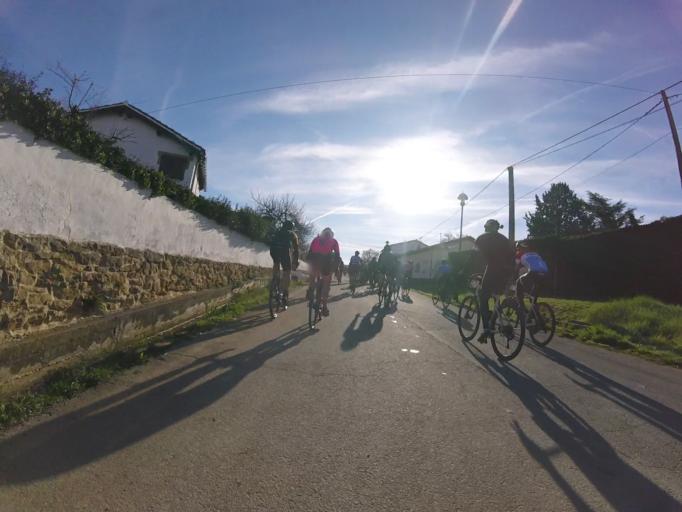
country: ES
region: Navarre
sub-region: Provincia de Navarra
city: Villatuerta
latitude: 42.6590
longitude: -1.9891
